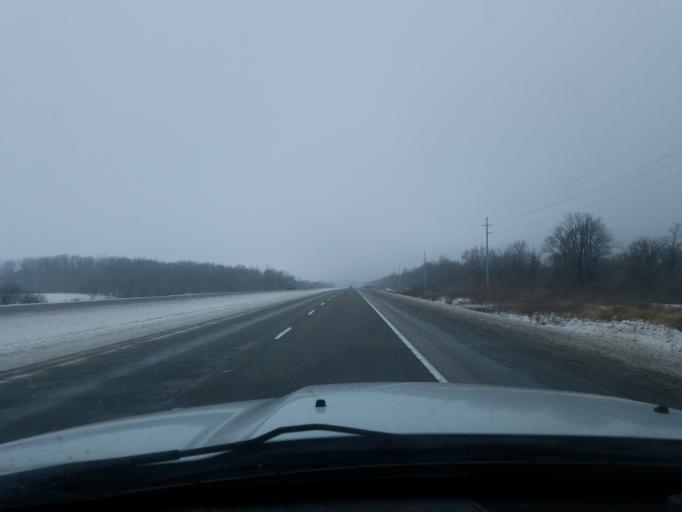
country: US
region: Indiana
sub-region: Fulton County
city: Rochester
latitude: 41.0161
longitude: -86.1717
